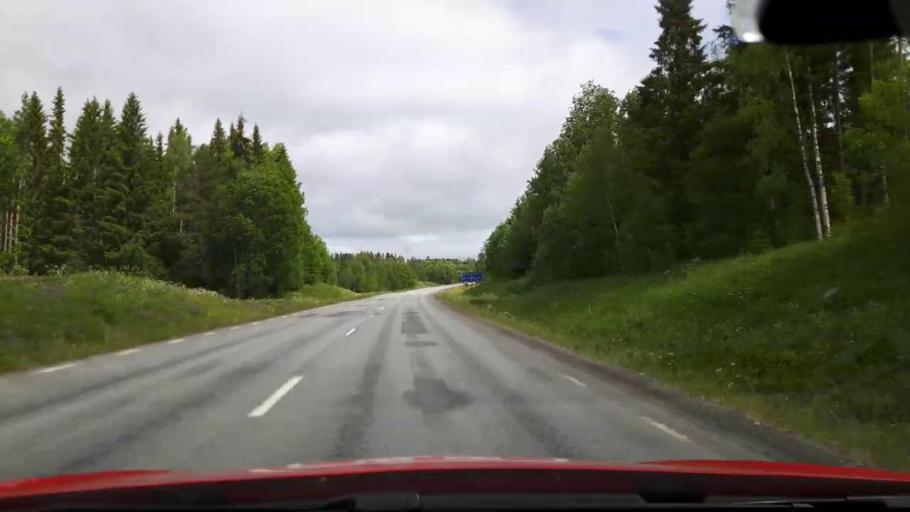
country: SE
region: Jaemtland
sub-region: Krokoms Kommun
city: Krokom
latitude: 63.3547
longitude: 14.4852
